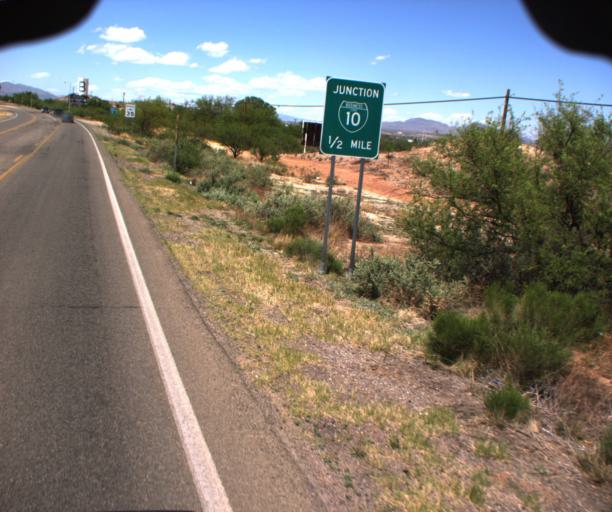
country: US
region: Arizona
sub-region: Cochise County
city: Benson
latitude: 31.9620
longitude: -110.2883
